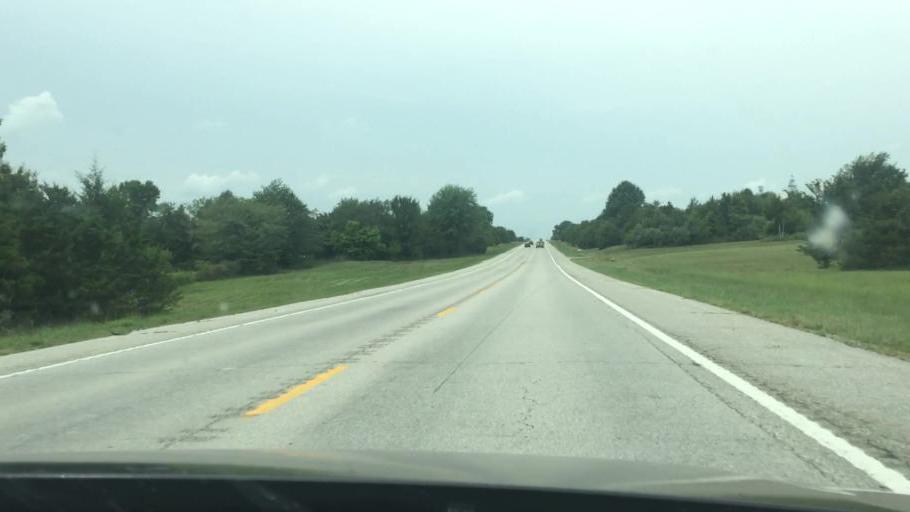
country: US
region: Missouri
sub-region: Moniteau County
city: Tipton
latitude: 38.6829
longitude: -92.9867
